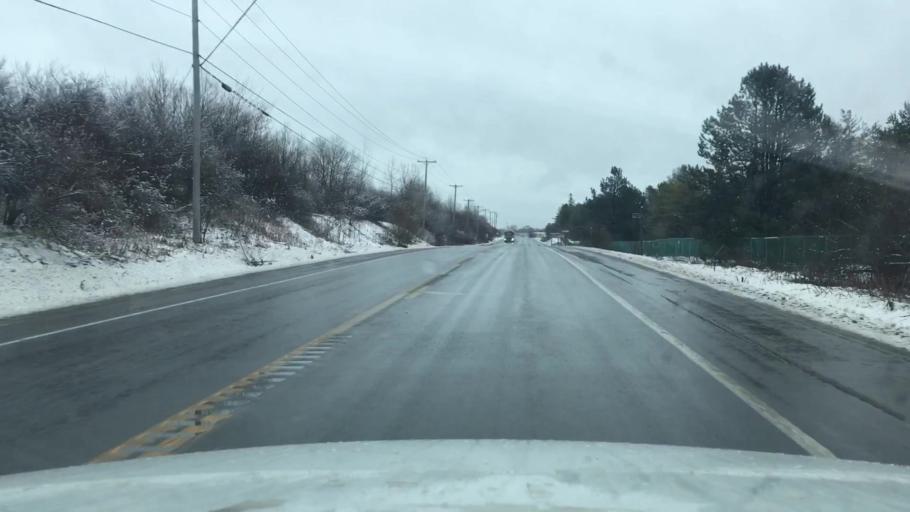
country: US
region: Maine
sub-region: Knox County
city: Thomaston
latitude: 44.0896
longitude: -69.1513
